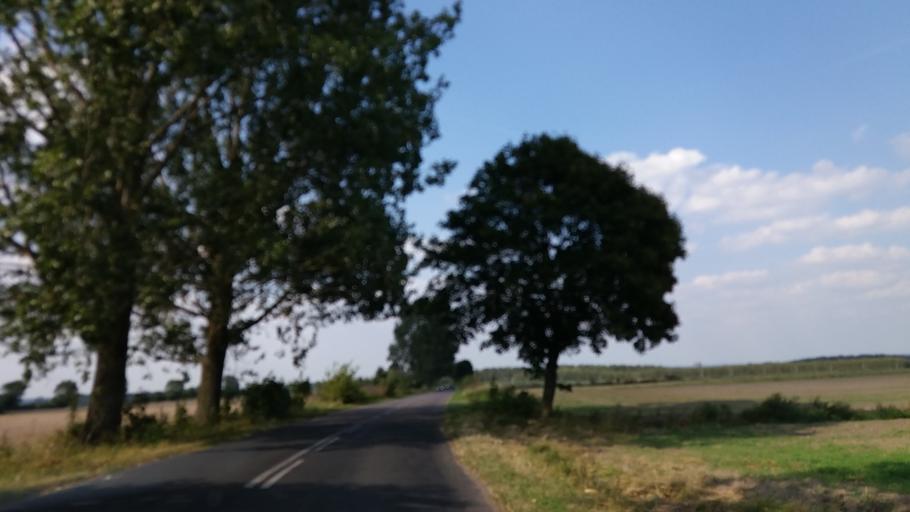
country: PL
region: West Pomeranian Voivodeship
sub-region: Powiat choszczenski
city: Krzecin
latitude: 53.1143
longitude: 15.4552
